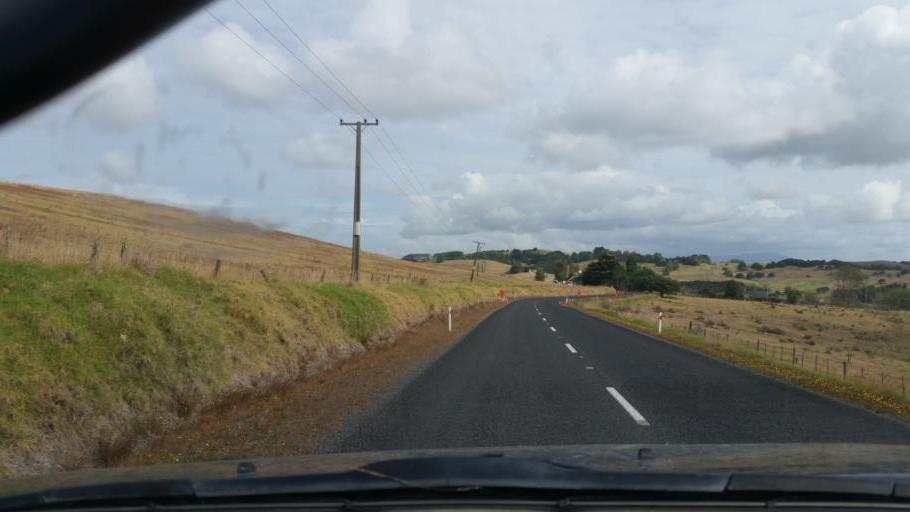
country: NZ
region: Northland
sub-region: Kaipara District
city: Dargaville
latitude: -35.9718
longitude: 173.9448
